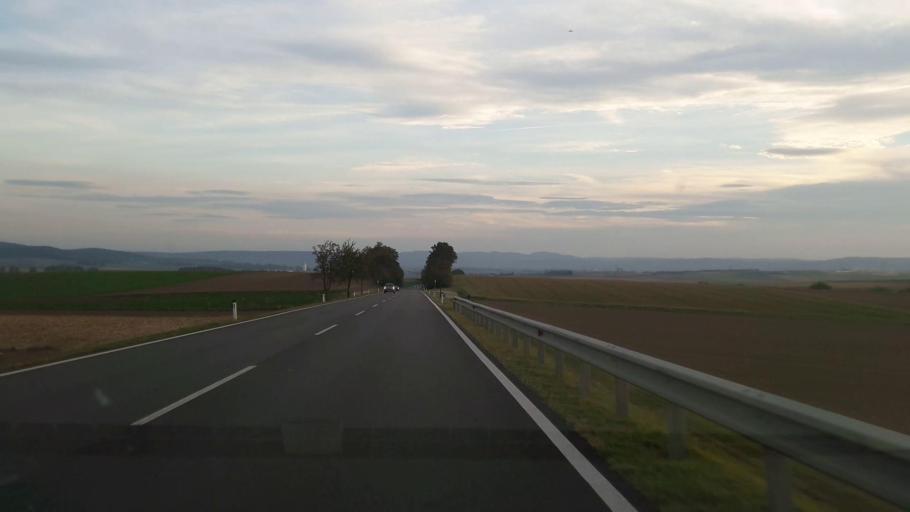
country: AT
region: Lower Austria
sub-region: Politischer Bezirk Korneuburg
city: Harmannsdorf
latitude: 48.4267
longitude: 16.3869
